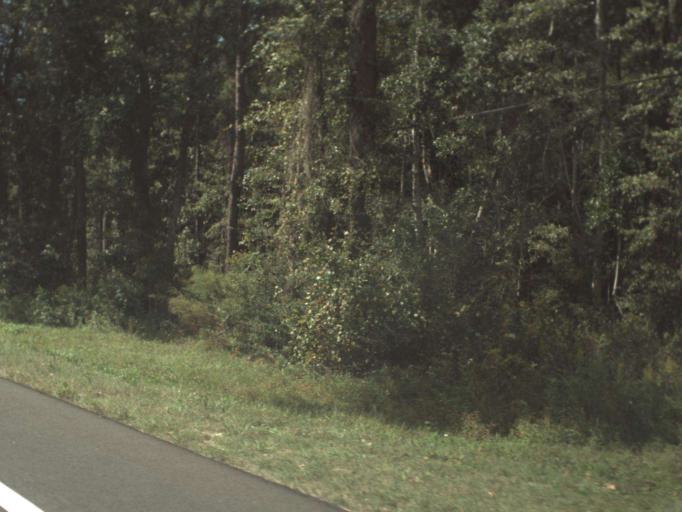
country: US
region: Florida
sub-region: Walton County
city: Freeport
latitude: 30.5089
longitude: -86.2008
